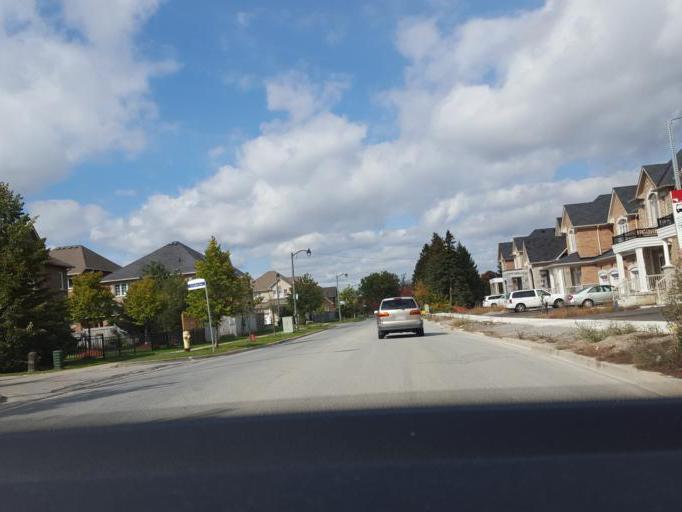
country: CA
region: Ontario
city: Markham
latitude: 43.8310
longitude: -79.2239
